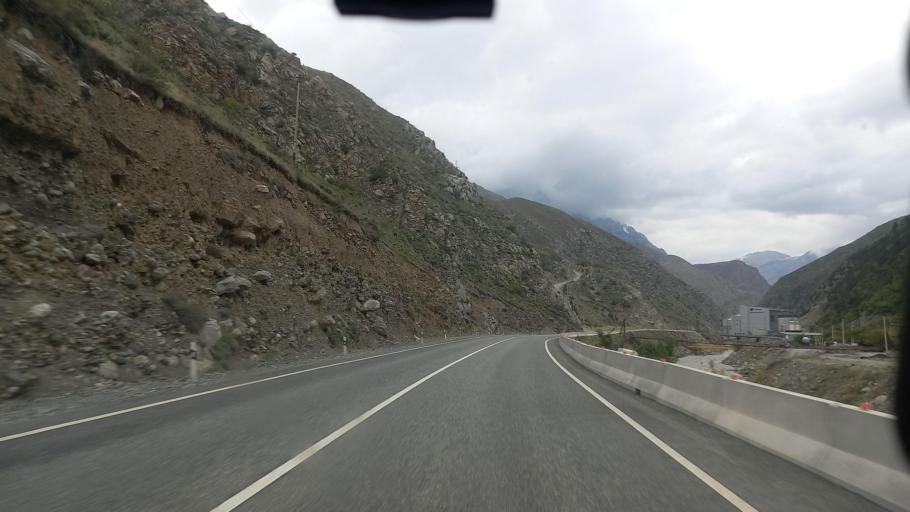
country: RU
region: North Ossetia
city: Mizur
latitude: 42.8423
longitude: 44.0344
